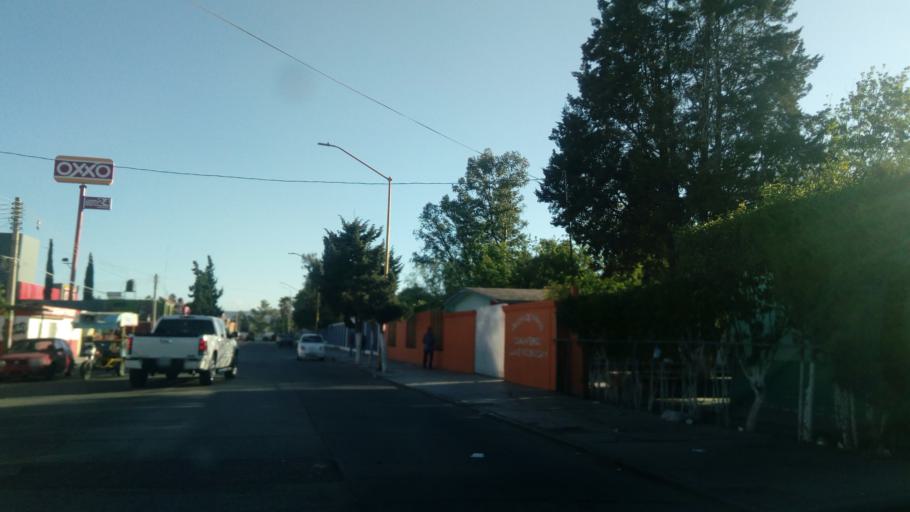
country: MX
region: Durango
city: Victoria de Durango
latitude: 24.0004
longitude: -104.6775
